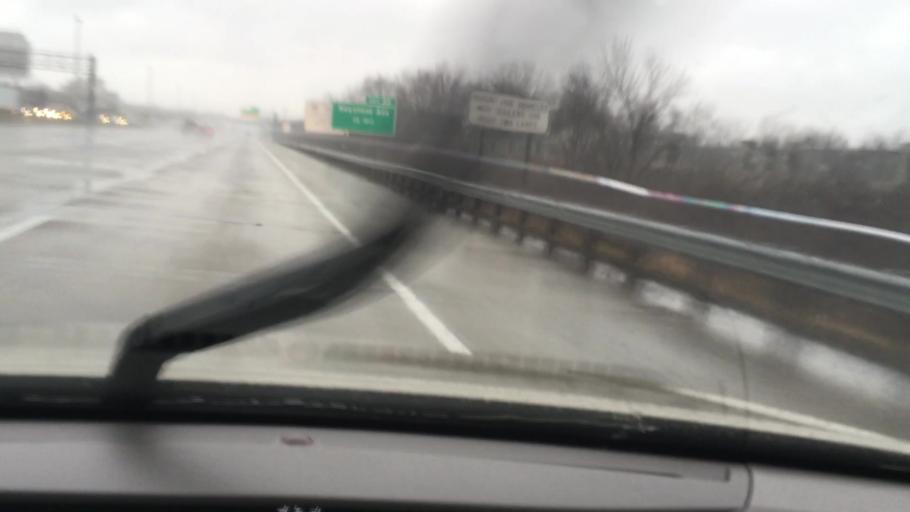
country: US
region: Indiana
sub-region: Hamilton County
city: Carmel
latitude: 39.9160
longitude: -86.0929
